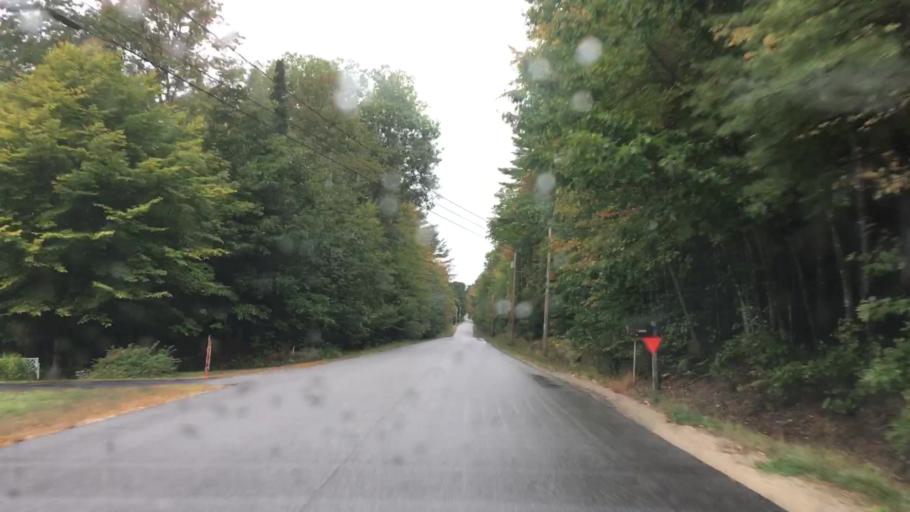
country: US
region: Maine
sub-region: Cumberland County
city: Harrison
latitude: 44.0829
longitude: -70.6460
